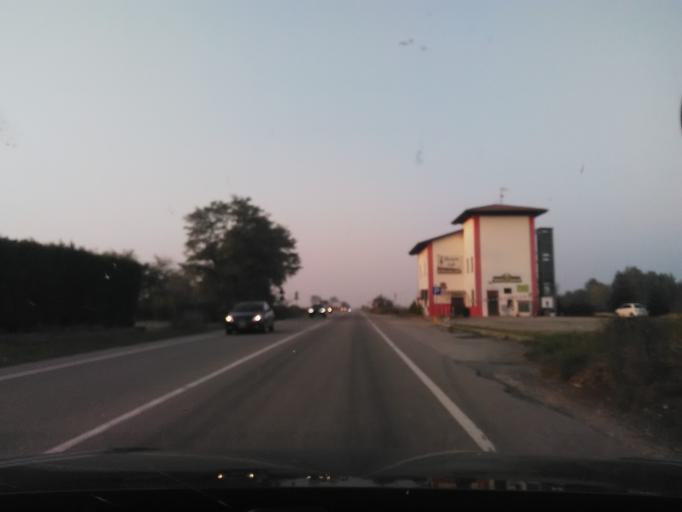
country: IT
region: Piedmont
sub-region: Provincia di Vercelli
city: Pezzana
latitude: 45.2592
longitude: 8.4640
